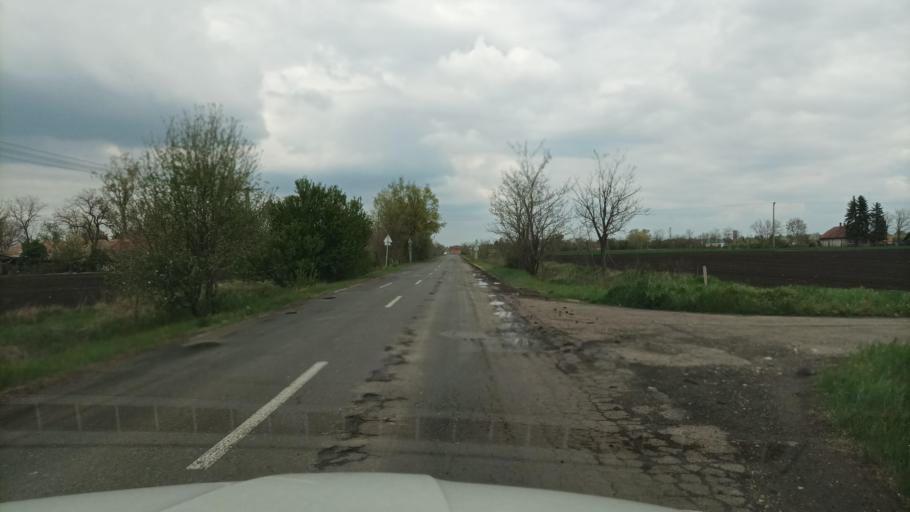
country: HU
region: Pest
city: Abony
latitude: 47.1755
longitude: 19.9895
